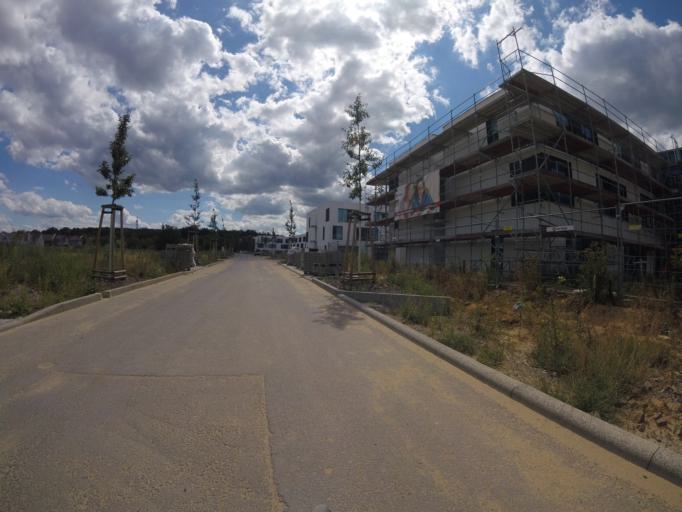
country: DE
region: Brandenburg
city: Werder
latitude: 52.4149
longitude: 12.9793
